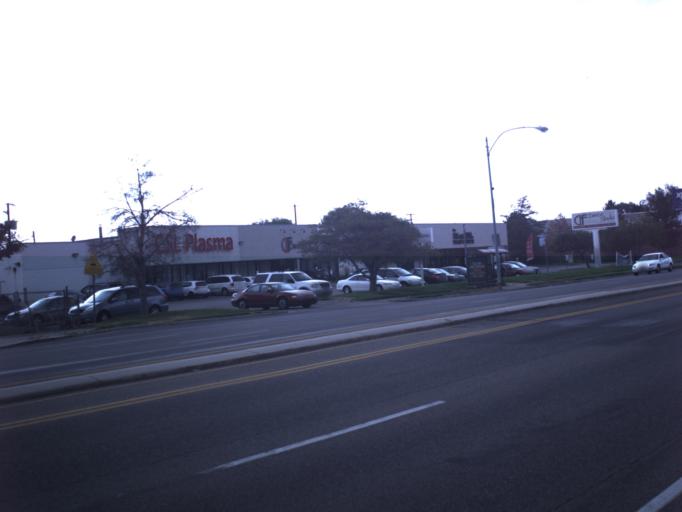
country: US
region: Utah
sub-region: Salt Lake County
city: South Salt Lake
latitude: 40.7060
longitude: -111.8882
